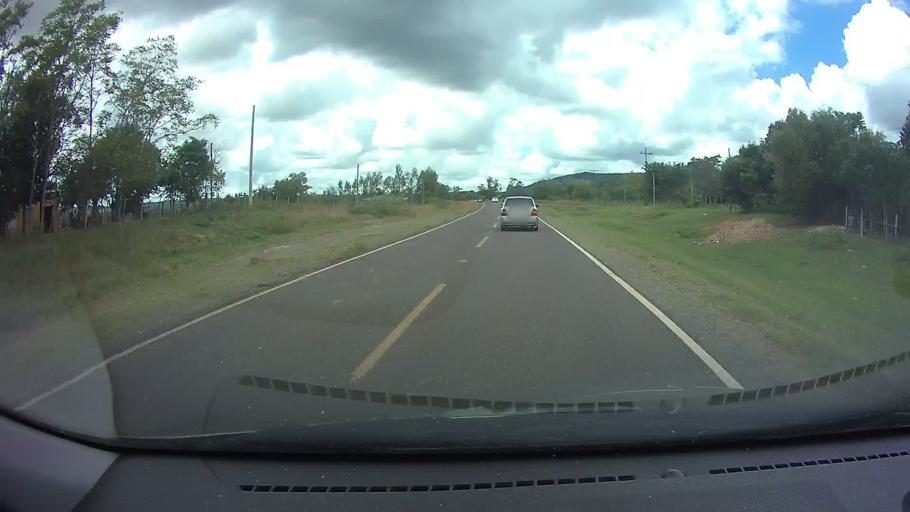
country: PY
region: Paraguari
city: Ybycui
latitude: -25.9104
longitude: -56.9917
